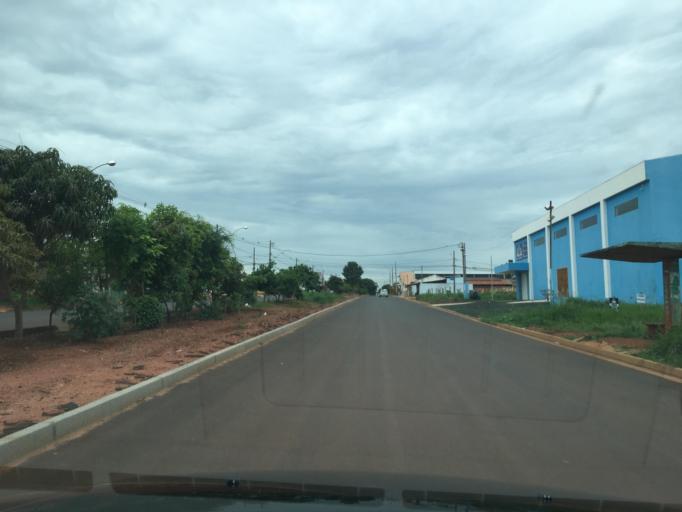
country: BR
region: Minas Gerais
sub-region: Uberlandia
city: Uberlandia
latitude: -18.8708
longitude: -48.2249
